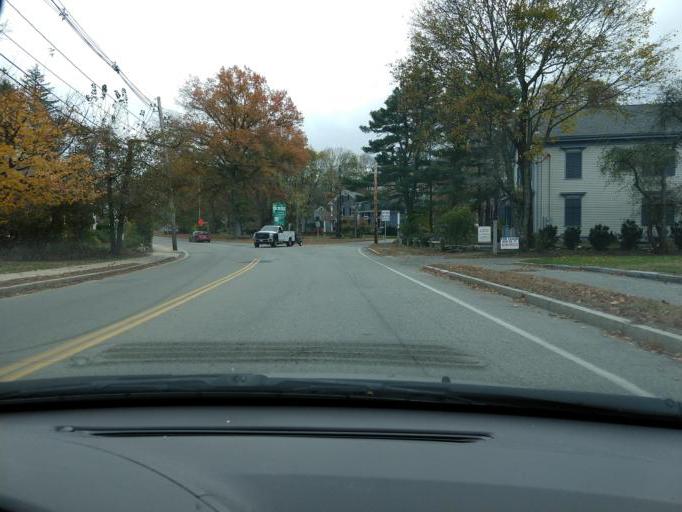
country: US
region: Massachusetts
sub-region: Middlesex County
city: Bedford
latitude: 42.4943
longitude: -71.2852
